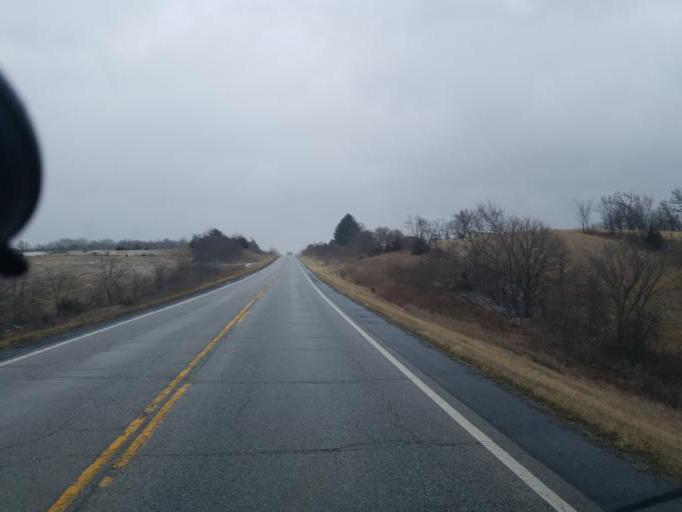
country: US
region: Missouri
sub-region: Putnam County
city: Unionville
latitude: 40.4711
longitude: -92.9343
